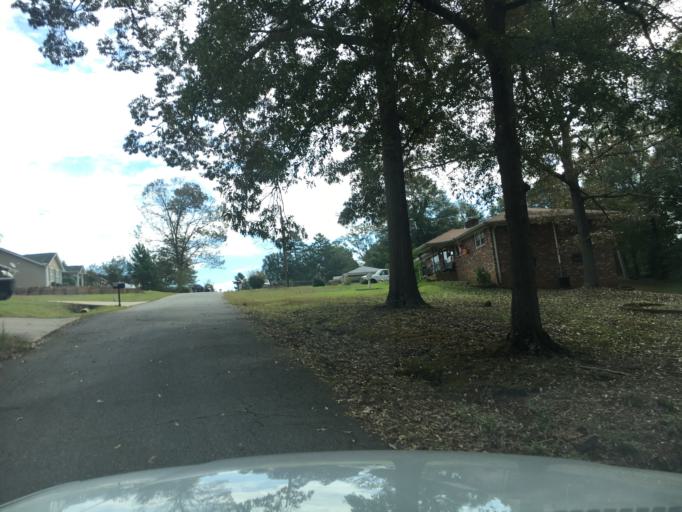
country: US
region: South Carolina
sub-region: Spartanburg County
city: Duncan
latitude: 34.9320
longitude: -82.1417
